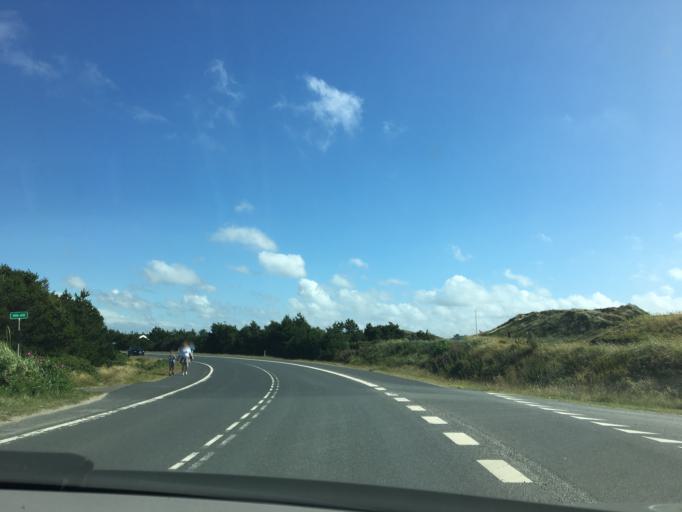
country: DK
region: South Denmark
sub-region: Varde Kommune
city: Oksbol
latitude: 55.7359
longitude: 8.1853
